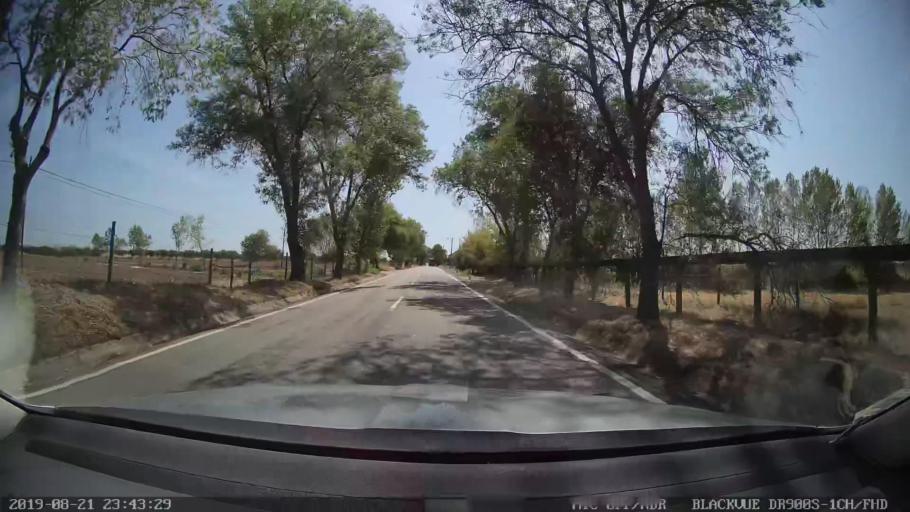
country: PT
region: Castelo Branco
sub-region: Idanha-A-Nova
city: Idanha-a-Nova
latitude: 39.8497
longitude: -7.2935
